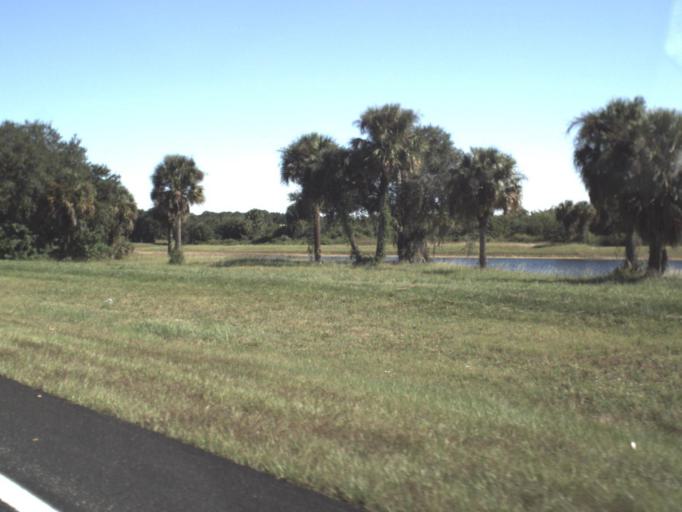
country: US
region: Florida
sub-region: Hendry County
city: Port LaBelle
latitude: 26.7684
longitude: -81.3722
